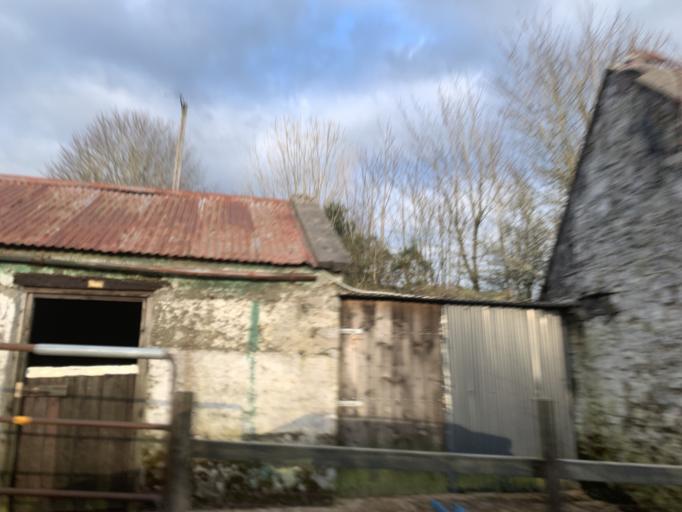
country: IE
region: Connaught
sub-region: Maigh Eo
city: Ballyhaunis
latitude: 53.8294
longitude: -8.7040
